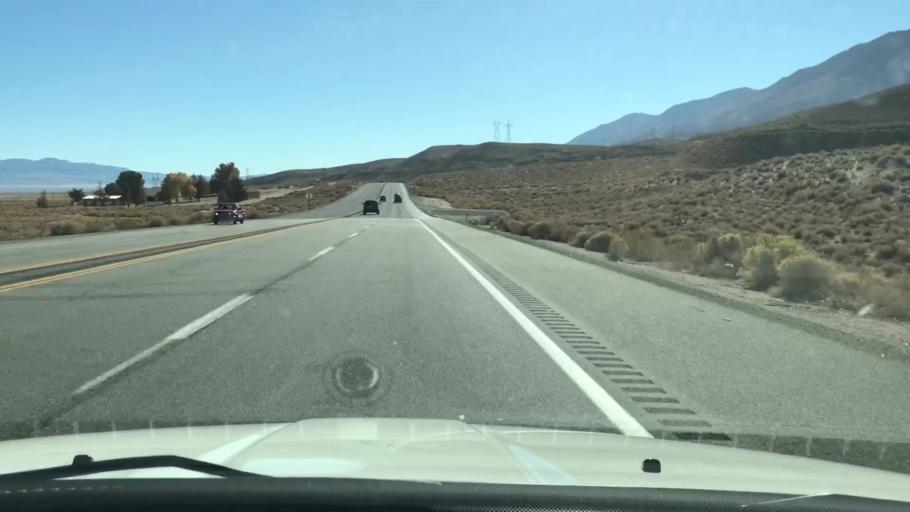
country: US
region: California
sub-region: Inyo County
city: Lone Pine
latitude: 36.5382
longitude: -118.0466
